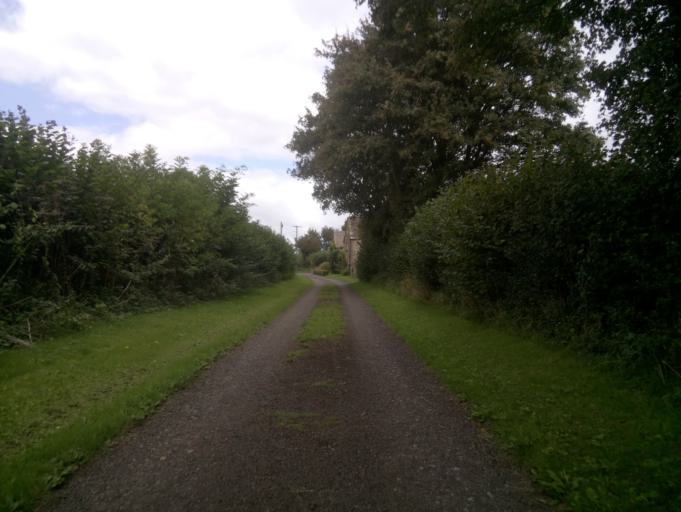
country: GB
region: England
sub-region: Wiltshire
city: Nettleton
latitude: 51.5091
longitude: -2.2275
